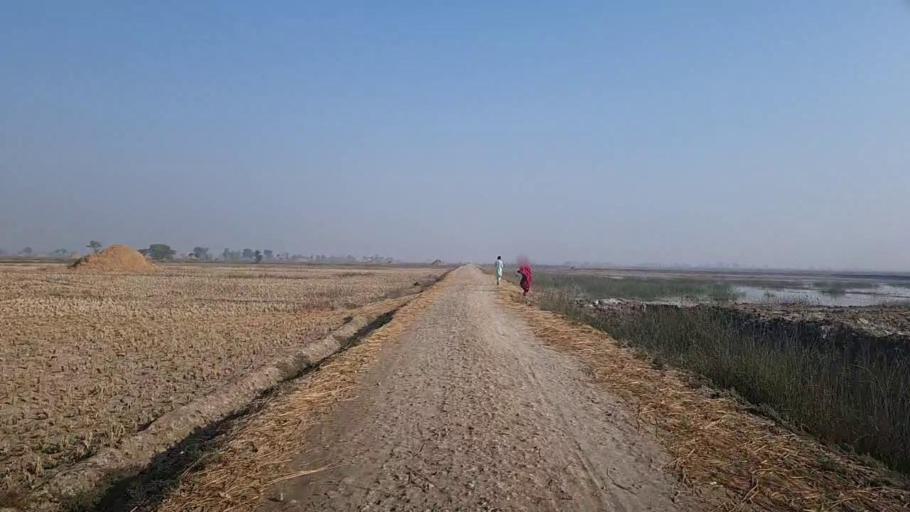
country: PK
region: Sindh
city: Radhan
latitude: 27.1358
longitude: 67.9052
